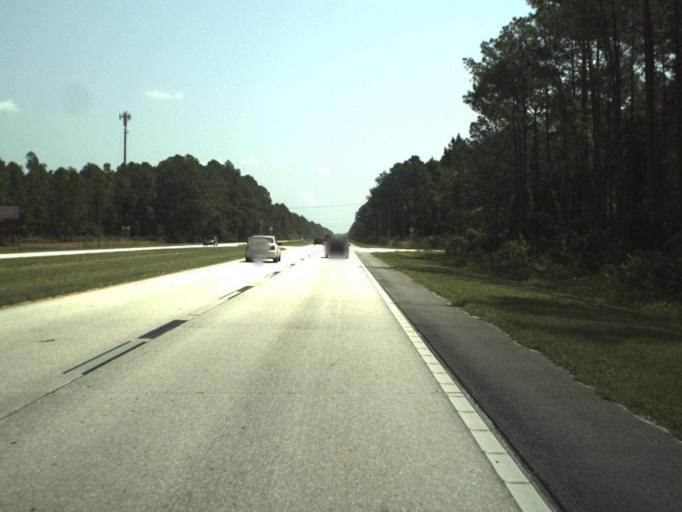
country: US
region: Florida
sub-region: Volusia County
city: North DeLand
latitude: 29.0724
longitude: -81.2510
